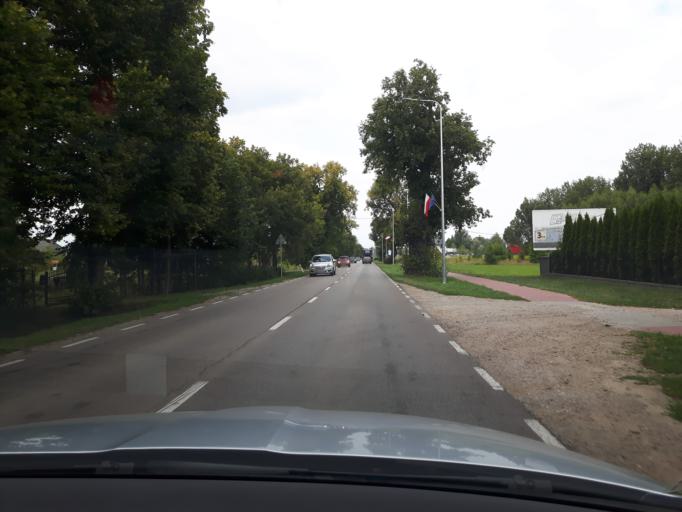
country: PL
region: Masovian Voivodeship
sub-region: Powiat legionowski
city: Nieporet
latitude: 52.4087
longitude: 21.0384
